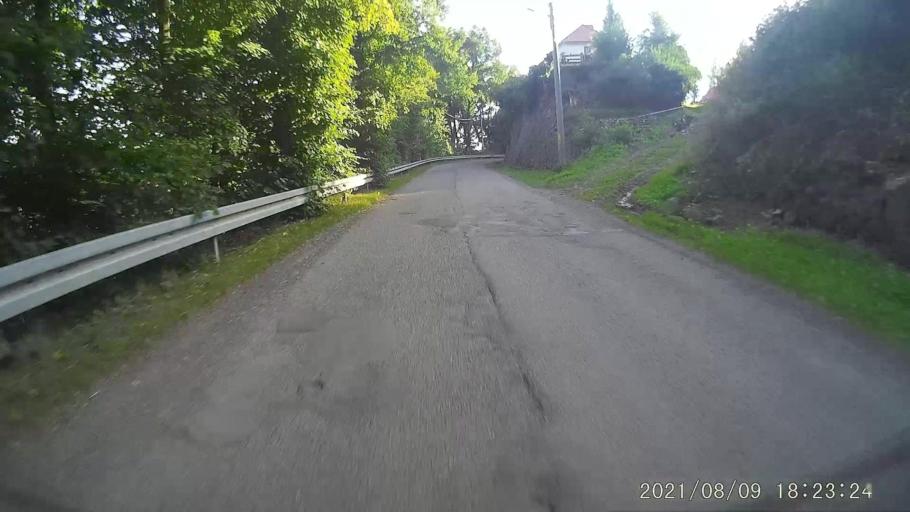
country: PL
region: Lower Silesian Voivodeship
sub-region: Powiat zabkowicki
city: Bardo
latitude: 50.5048
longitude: 16.7206
